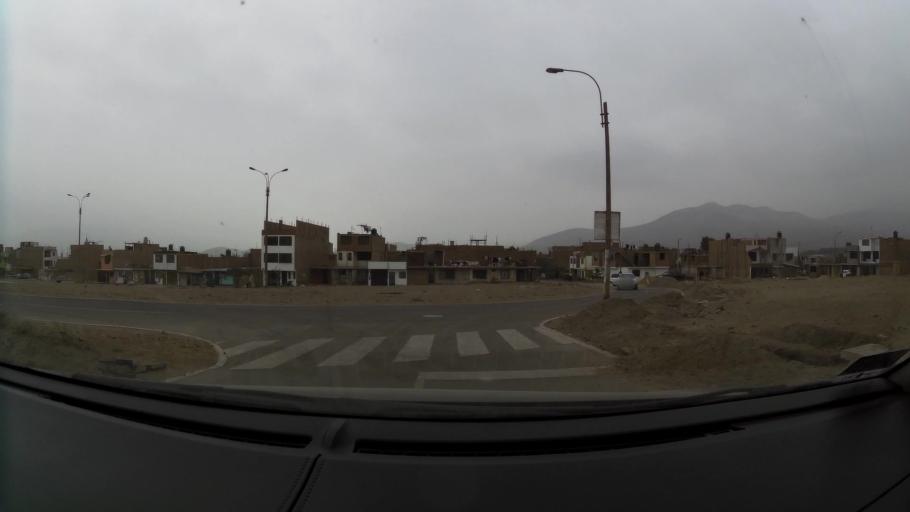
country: PE
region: Lima
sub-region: Lima
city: Santa Rosa
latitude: -11.7907
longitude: -77.1551
